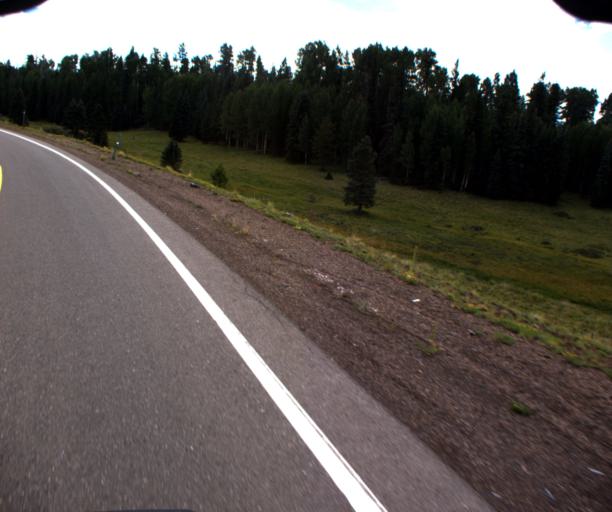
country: US
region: Arizona
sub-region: Apache County
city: Eagar
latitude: 34.0054
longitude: -109.5658
